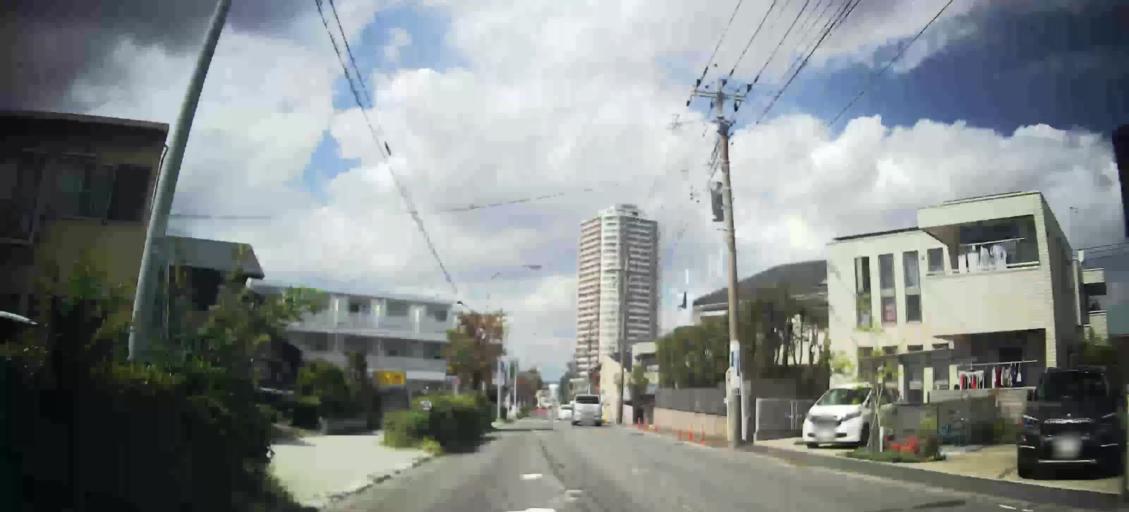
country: JP
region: Kanagawa
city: Yokohama
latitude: 35.4726
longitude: 139.5521
